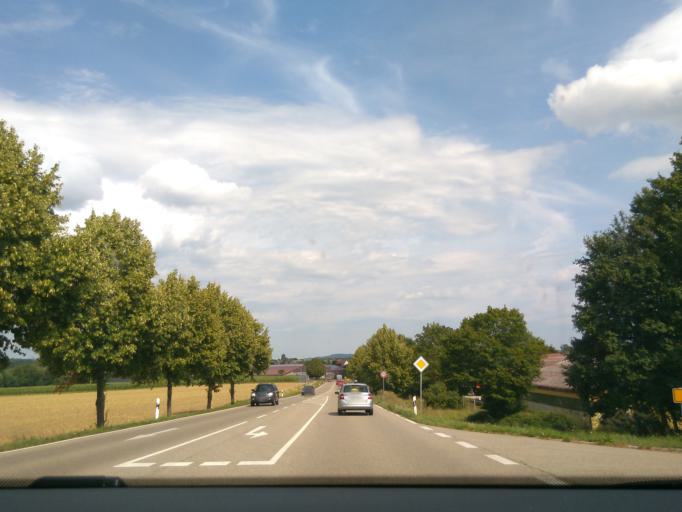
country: DE
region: Baden-Wuerttemberg
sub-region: Regierungsbezirk Stuttgart
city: Michelfeld
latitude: 49.0959
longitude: 9.6670
